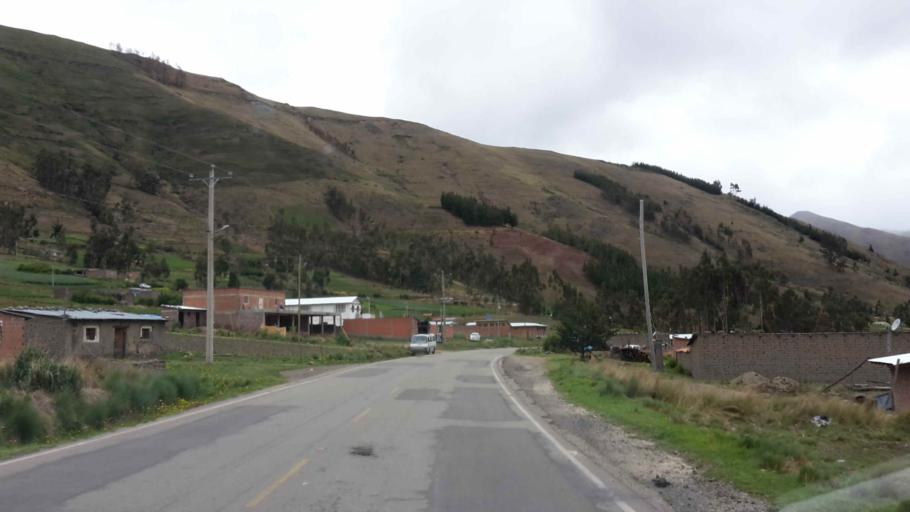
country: BO
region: Cochabamba
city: Arani
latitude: -17.4813
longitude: -65.5457
